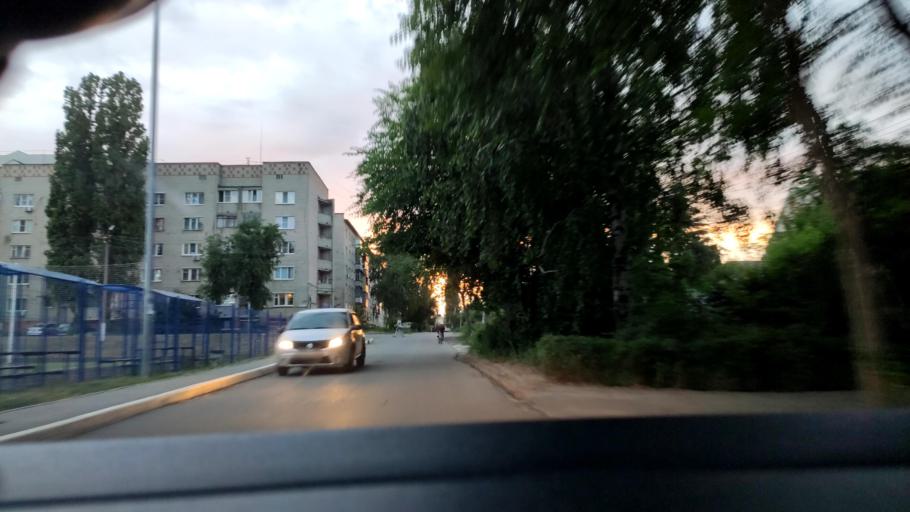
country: RU
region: Voronezj
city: Semiluki
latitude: 51.6947
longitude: 39.0248
